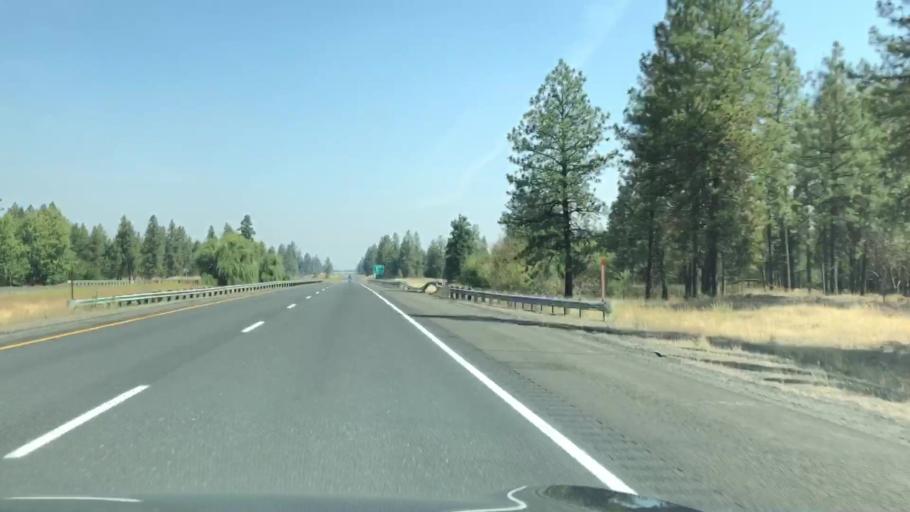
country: US
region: Washington
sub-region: Spokane County
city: Medical Lake
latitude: 47.4893
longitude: -117.7125
